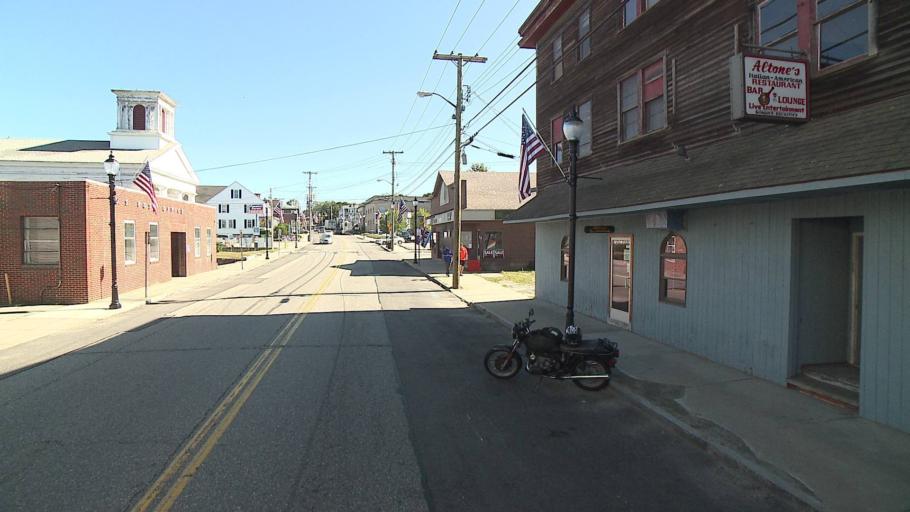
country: US
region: Connecticut
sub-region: New London County
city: Jewett City
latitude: 41.6057
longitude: -71.9827
